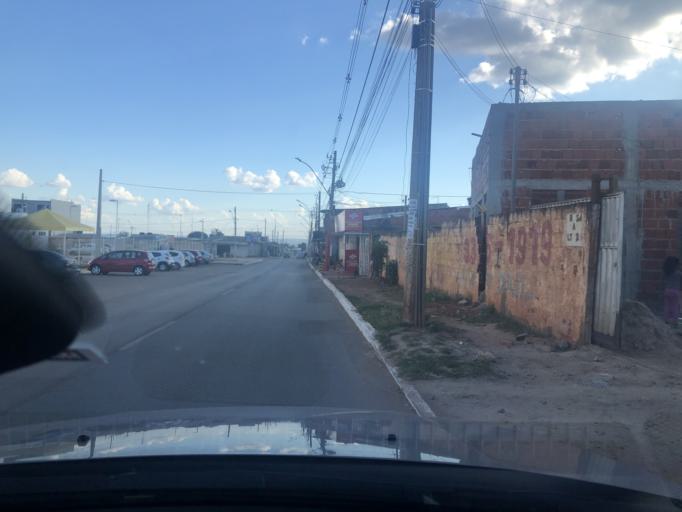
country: BR
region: Federal District
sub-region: Brasilia
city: Brasilia
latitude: -15.8339
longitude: -48.1335
